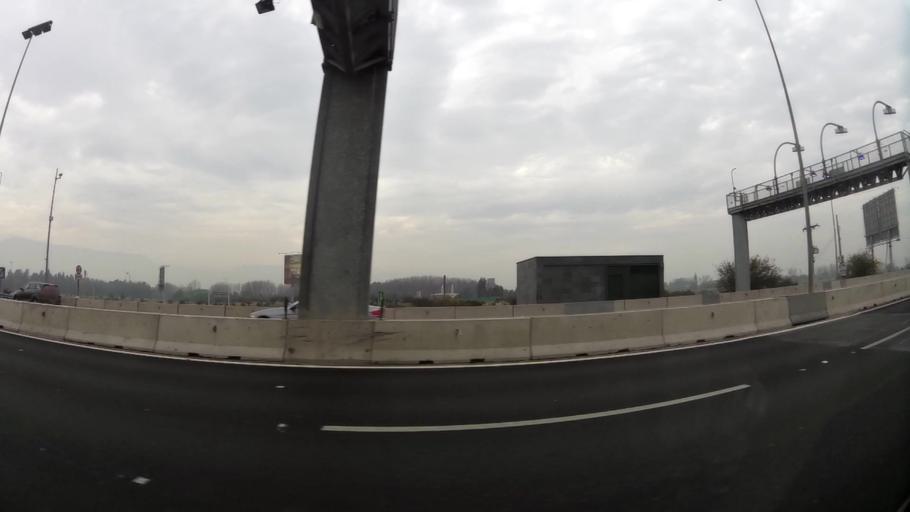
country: CL
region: Santiago Metropolitan
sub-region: Provincia de Santiago
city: Lo Prado
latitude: -33.4179
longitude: -70.7907
